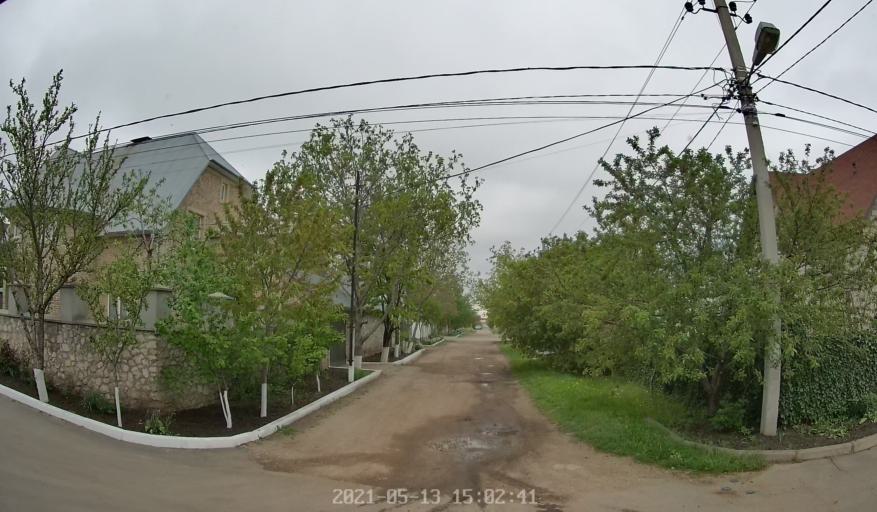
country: MD
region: Chisinau
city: Stauceni
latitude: 47.1032
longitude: 28.8689
